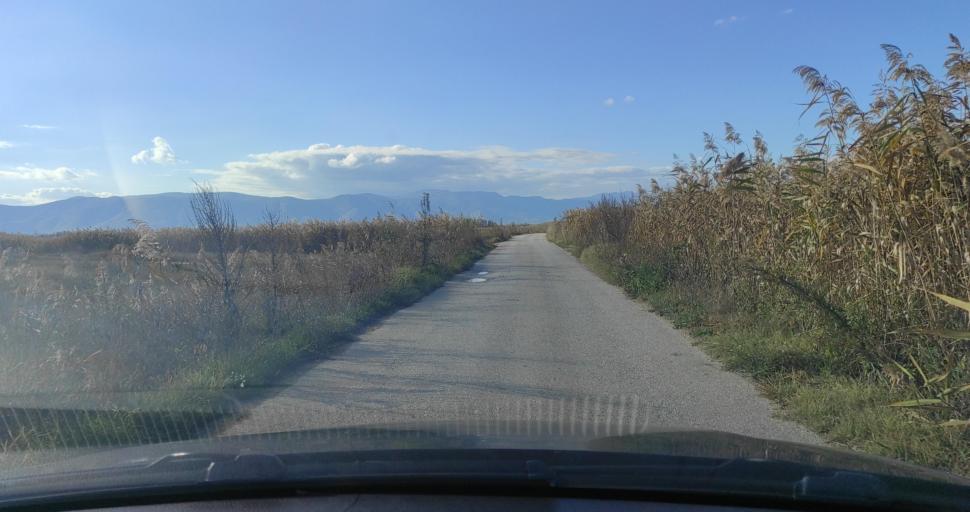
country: MK
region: Prilep
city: Topolcani
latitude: 41.2807
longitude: 21.4245
